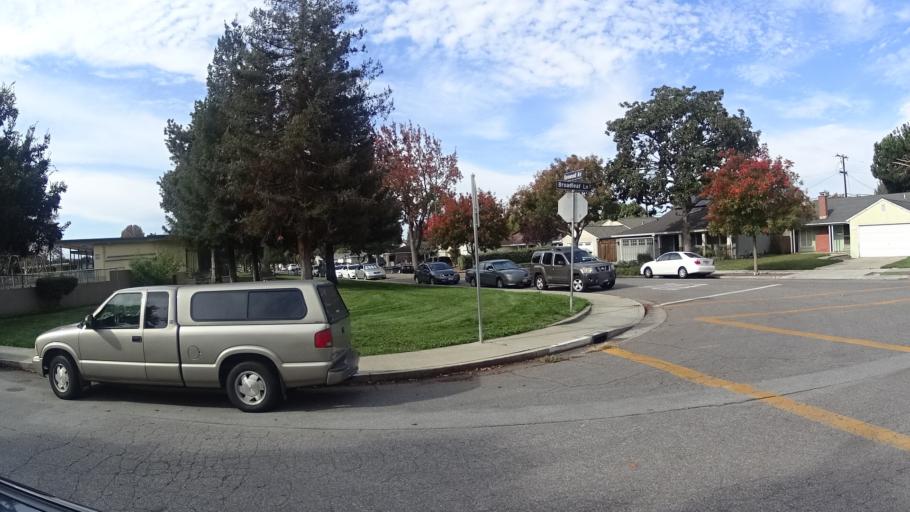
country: US
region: California
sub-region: Santa Clara County
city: Burbank
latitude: 37.3326
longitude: -121.9411
